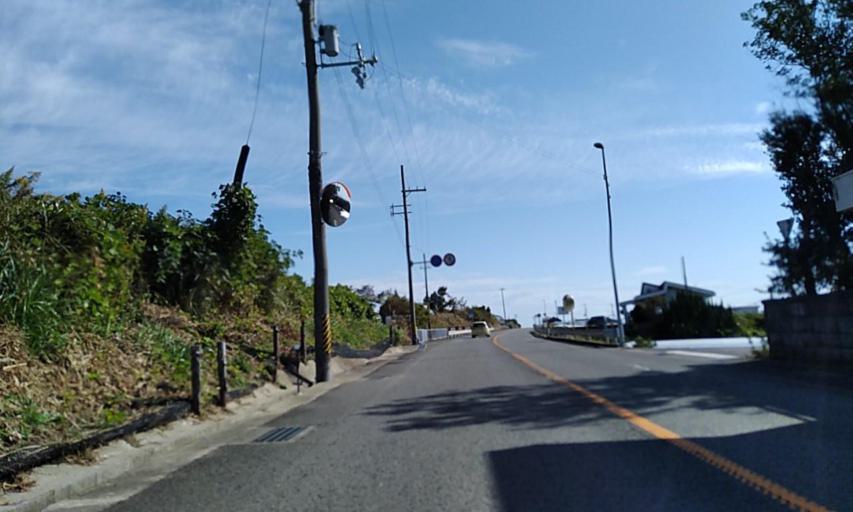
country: JP
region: Wakayama
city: Gobo
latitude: 33.8249
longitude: 135.1898
